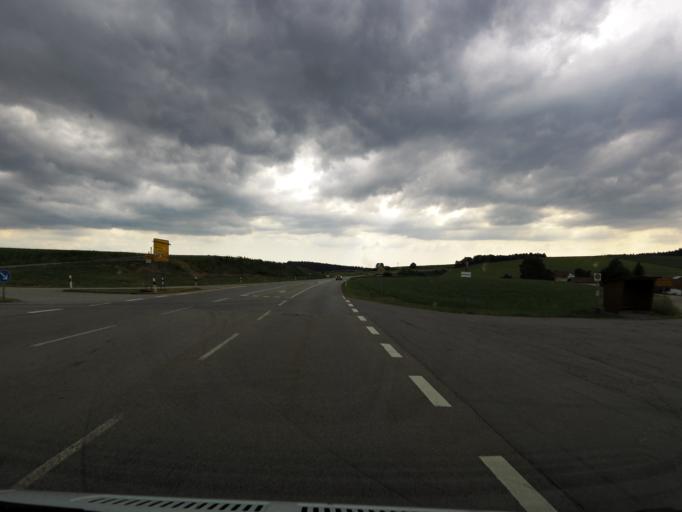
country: DE
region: Bavaria
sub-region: Lower Bavaria
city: Buchlberg
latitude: 48.6913
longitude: 13.5093
